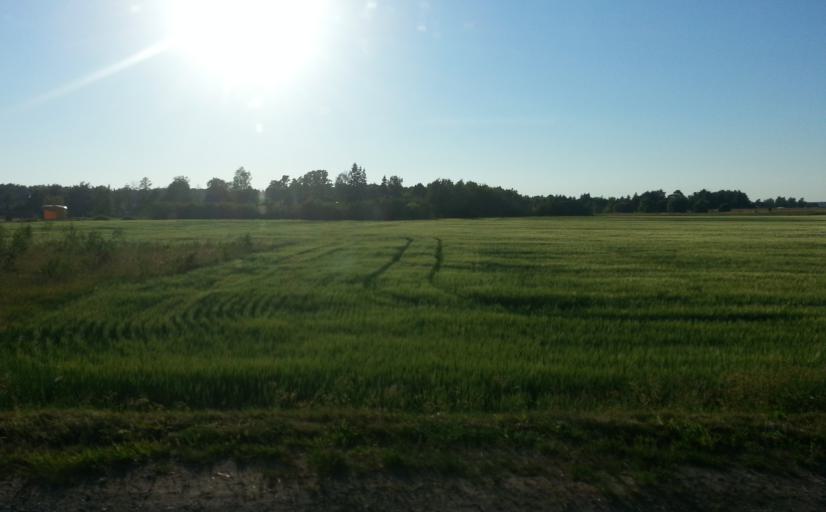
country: LT
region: Panevezys
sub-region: Panevezys City
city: Panevezys
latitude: 55.7842
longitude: 24.3688
